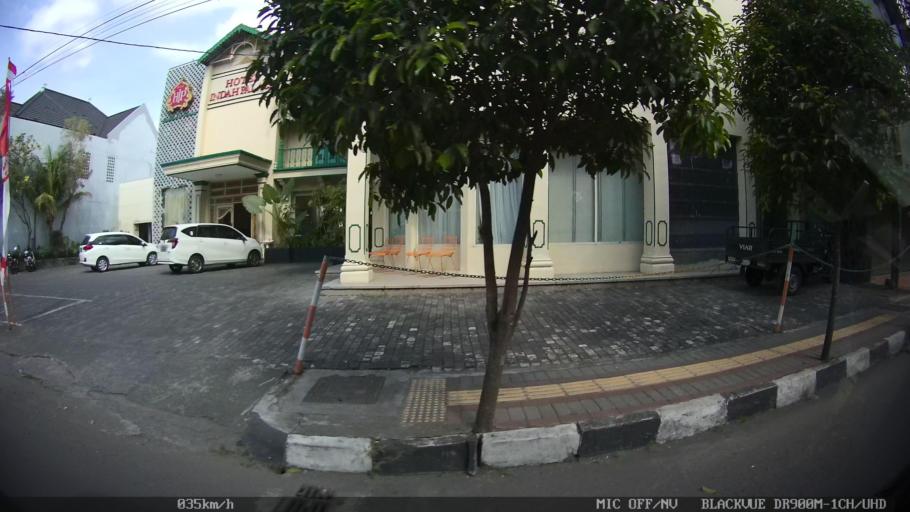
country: ID
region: Daerah Istimewa Yogyakarta
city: Yogyakarta
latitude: -7.8186
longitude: 110.3730
